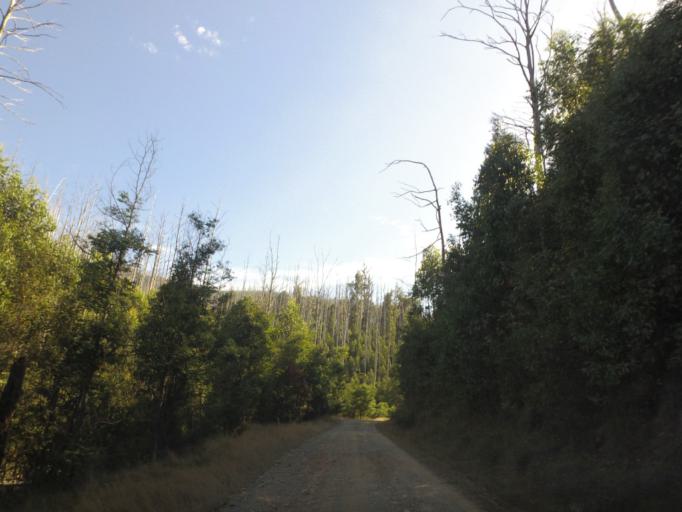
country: AU
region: Victoria
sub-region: Yarra Ranges
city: Millgrove
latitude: -37.5017
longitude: 145.7985
